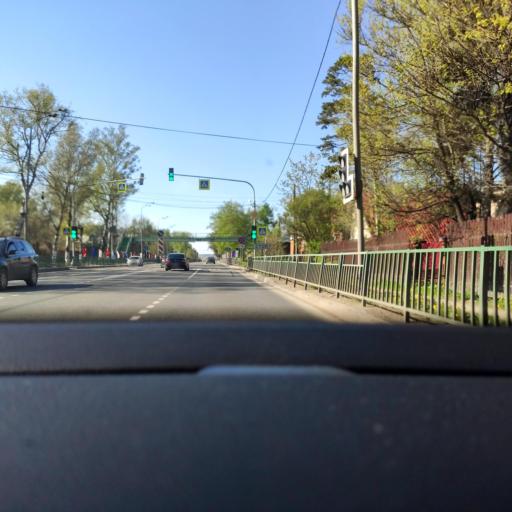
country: RU
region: Moskovskaya
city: Dedenevo
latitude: 56.2441
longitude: 37.5237
